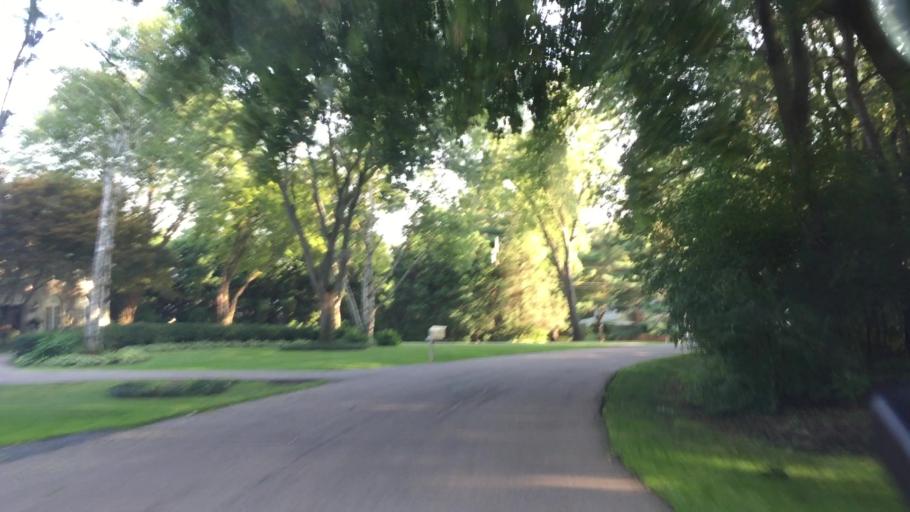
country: US
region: Michigan
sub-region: Oakland County
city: Bloomfield Hills
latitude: 42.5607
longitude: -83.2697
